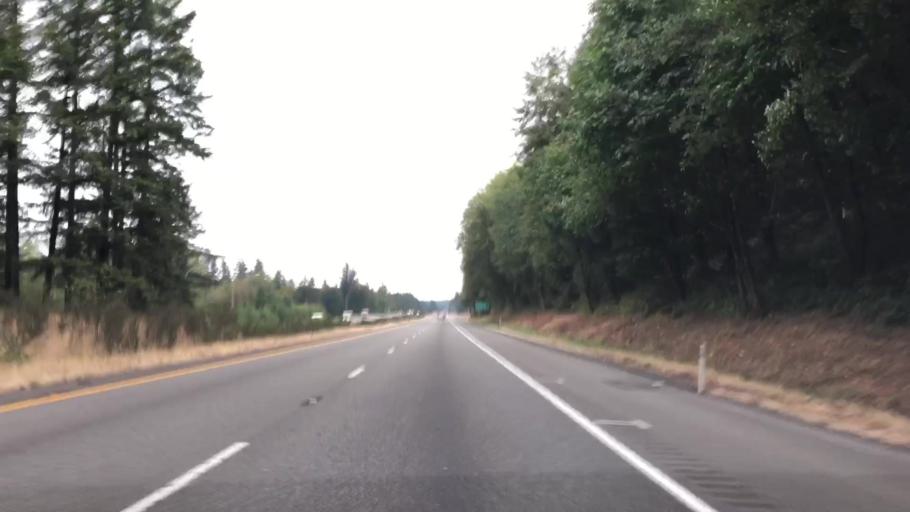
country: US
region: Washington
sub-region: Kitsap County
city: Burley
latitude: 47.4257
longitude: -122.6233
